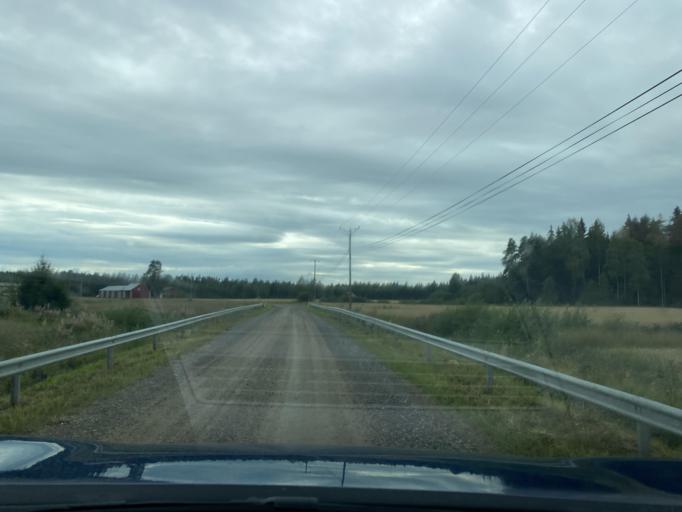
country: FI
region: Pirkanmaa
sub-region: Lounais-Pirkanmaa
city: Punkalaidun
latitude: 61.2339
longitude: 23.0413
